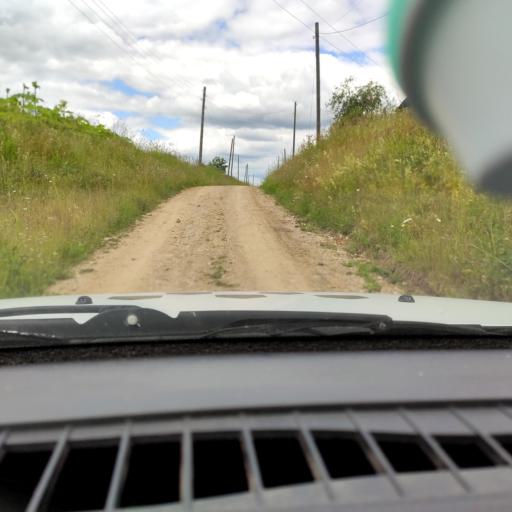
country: RU
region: Perm
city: Suksun
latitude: 57.2100
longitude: 57.7018
